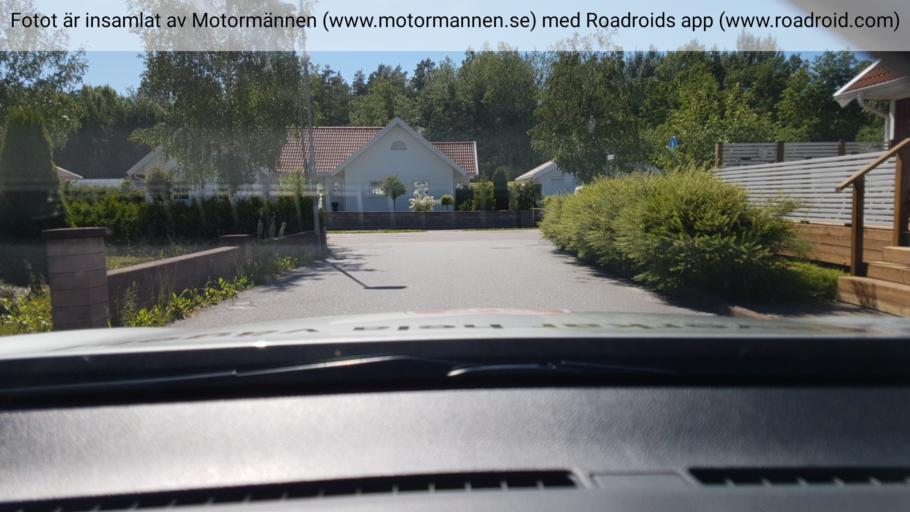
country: SE
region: OErebro
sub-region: Kumla Kommun
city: Kumla
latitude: 59.1490
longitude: 15.1428
